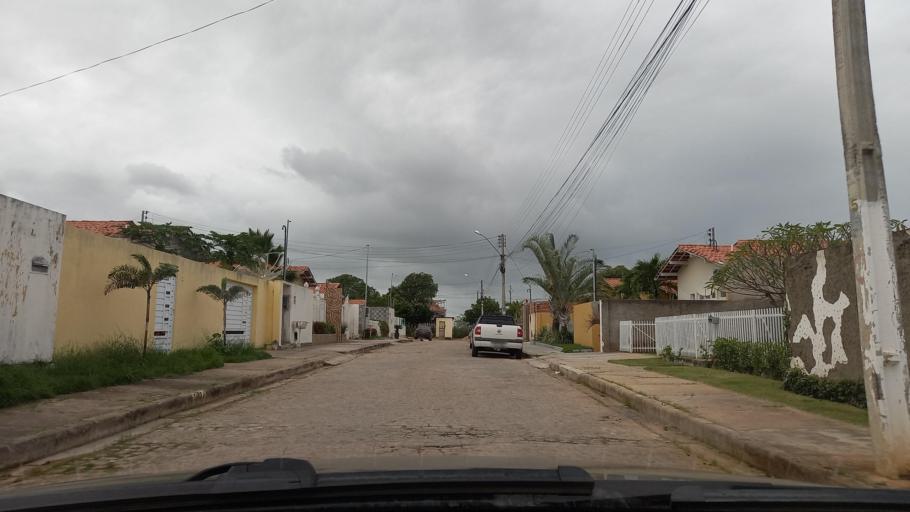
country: BR
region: Sergipe
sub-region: Caninde De Sao Francisco
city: Caninde de Sao Francisco
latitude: -9.6157
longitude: -37.7662
